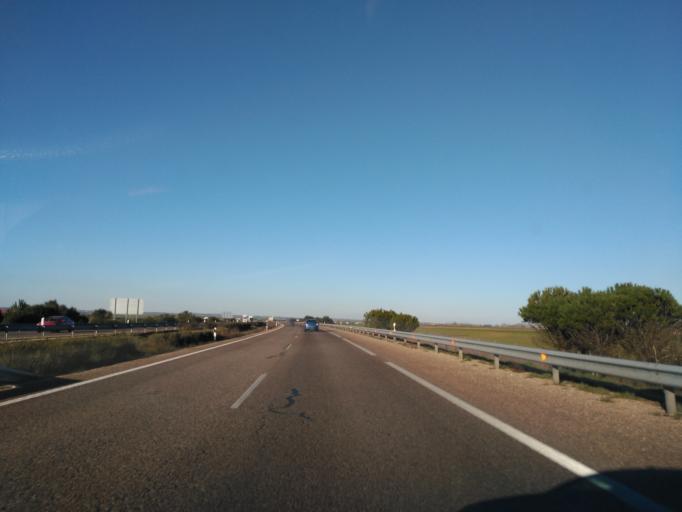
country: ES
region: Castille and Leon
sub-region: Provincia de Salamanca
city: Gomecello
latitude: 41.0363
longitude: -5.5637
